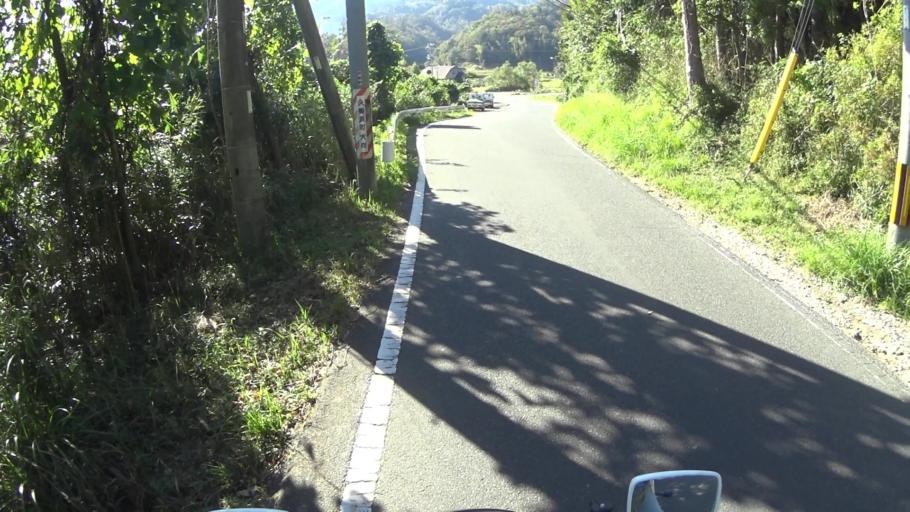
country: JP
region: Hyogo
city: Toyooka
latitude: 35.6377
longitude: 134.8918
